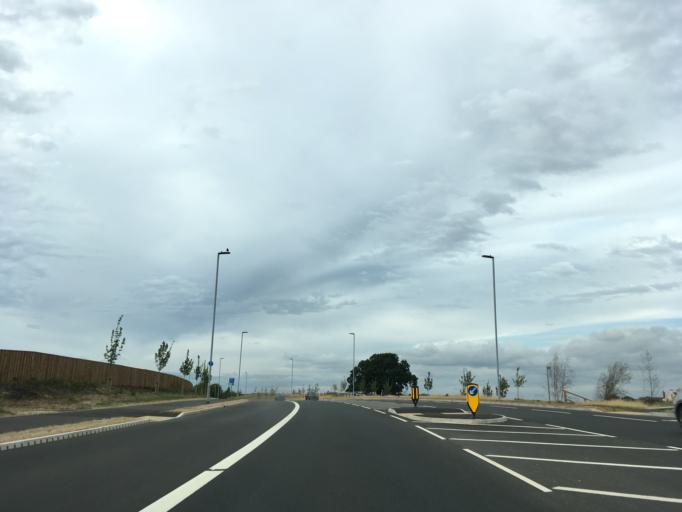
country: GB
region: England
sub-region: South Gloucestershire
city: Stoke Gifford
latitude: 51.5145
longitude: -2.5285
